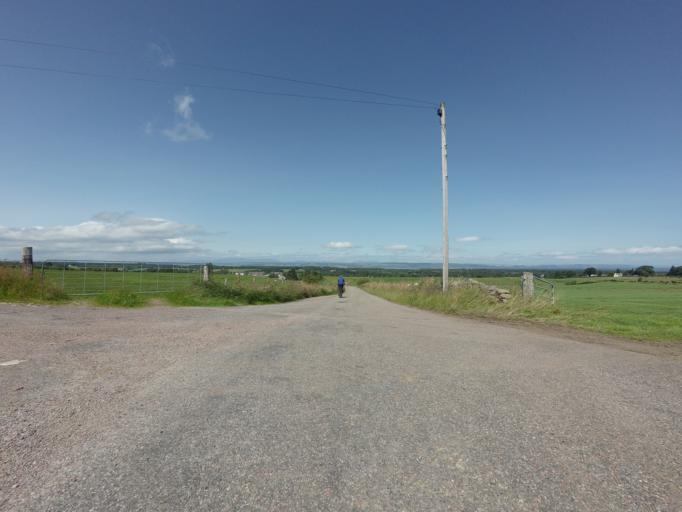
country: GB
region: Scotland
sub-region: Highland
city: Nairn
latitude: 57.5007
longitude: -3.9783
